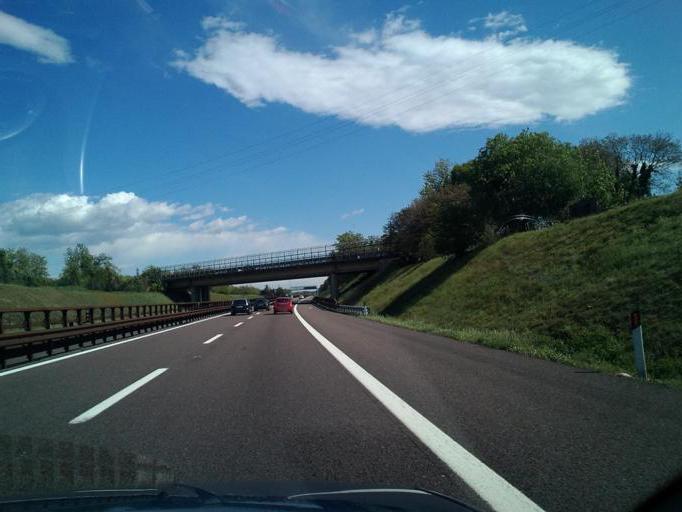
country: IT
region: Veneto
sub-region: Provincia di Verona
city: Bassone
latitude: 45.4473
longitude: 10.8867
